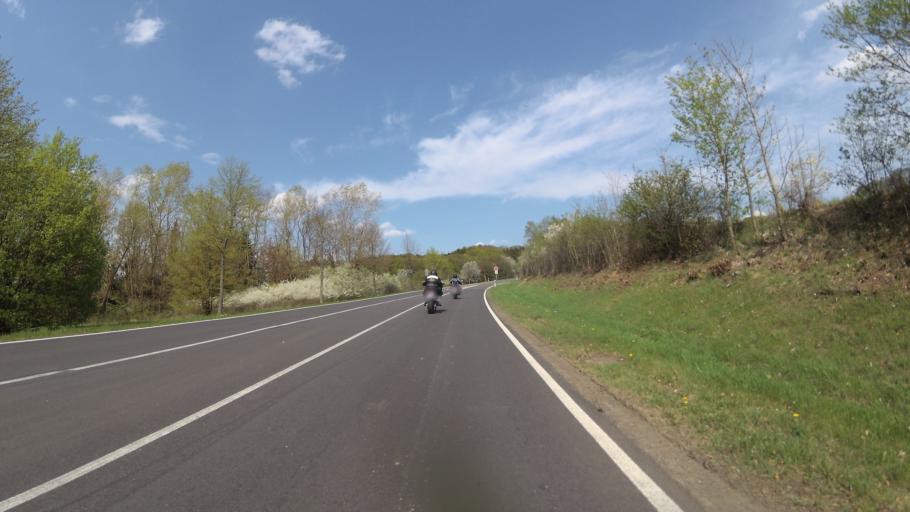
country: DE
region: Rheinland-Pfalz
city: Mullenbach
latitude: 50.3210
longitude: 6.9202
